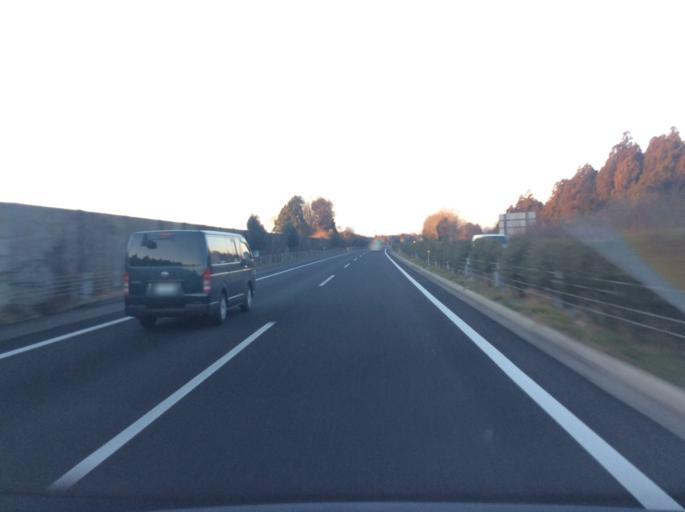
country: JP
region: Ibaraki
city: Funaishikawa
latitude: 36.4609
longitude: 140.4868
